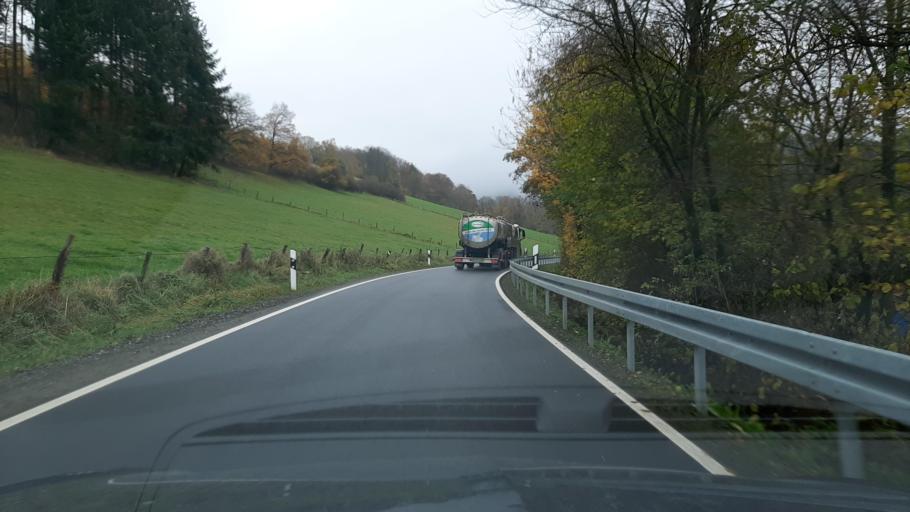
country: DE
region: North Rhine-Westphalia
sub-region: Regierungsbezirk Arnsberg
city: Bad Fredeburg
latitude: 51.1641
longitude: 8.3456
